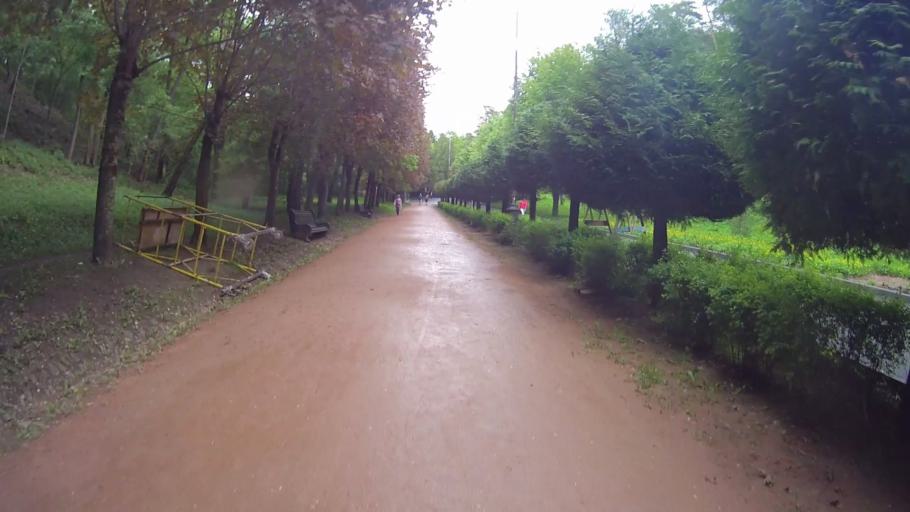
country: RU
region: Stavropol'skiy
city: Kislovodsk
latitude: 43.8960
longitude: 42.7255
